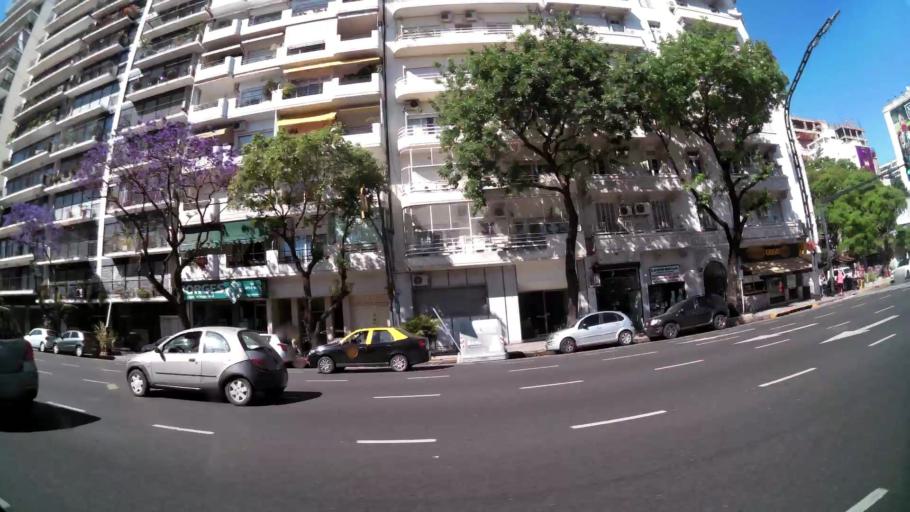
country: AR
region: Buenos Aires F.D.
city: Colegiales
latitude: -34.5640
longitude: -58.4361
